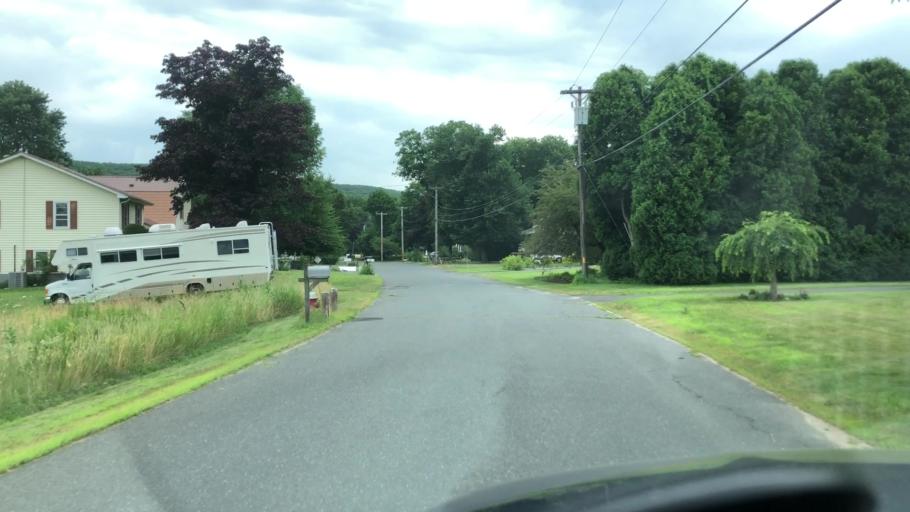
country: US
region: Massachusetts
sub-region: Hampshire County
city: Easthampton
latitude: 42.2435
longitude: -72.6629
